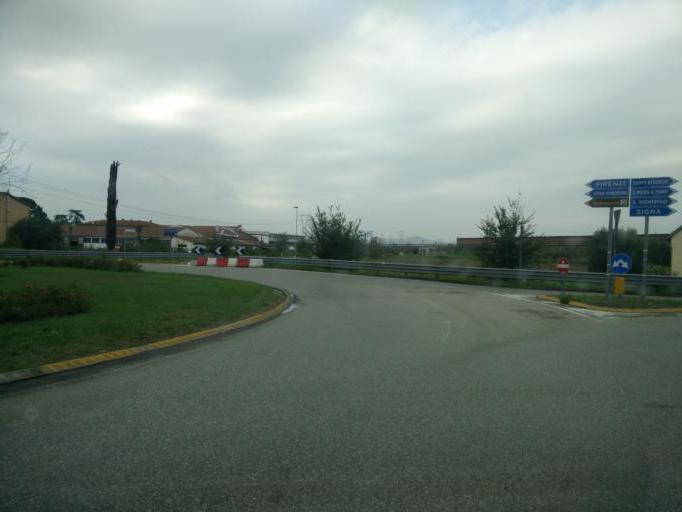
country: IT
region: Tuscany
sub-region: Province of Florence
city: San Donnino
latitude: 43.8156
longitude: 11.1538
